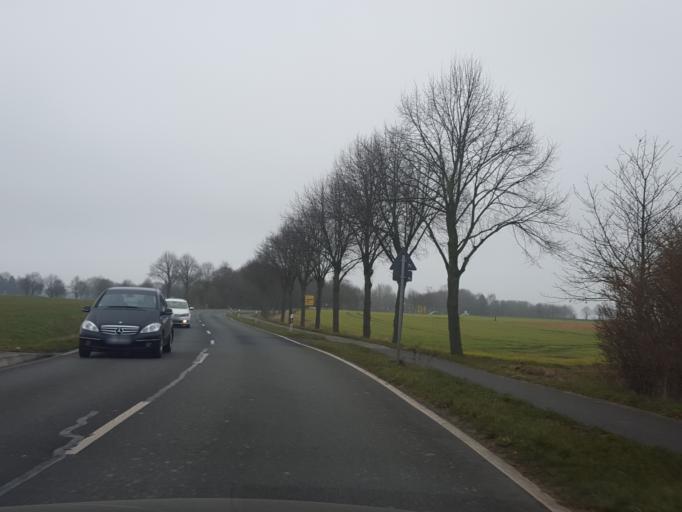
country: DE
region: North Rhine-Westphalia
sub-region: Regierungsbezirk Munster
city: Recklinghausen
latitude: 51.6354
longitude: 7.2242
